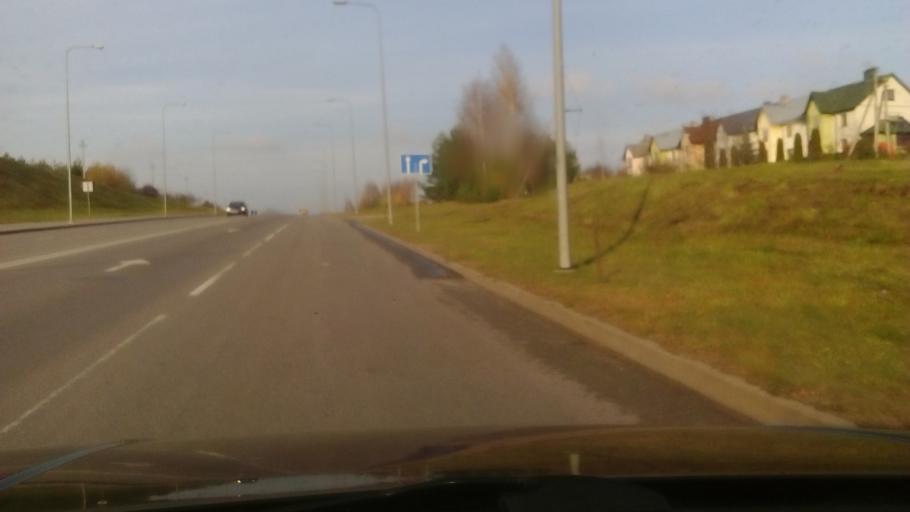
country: LT
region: Alytaus apskritis
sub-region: Alytus
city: Alytus
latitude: 54.3932
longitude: 23.9988
